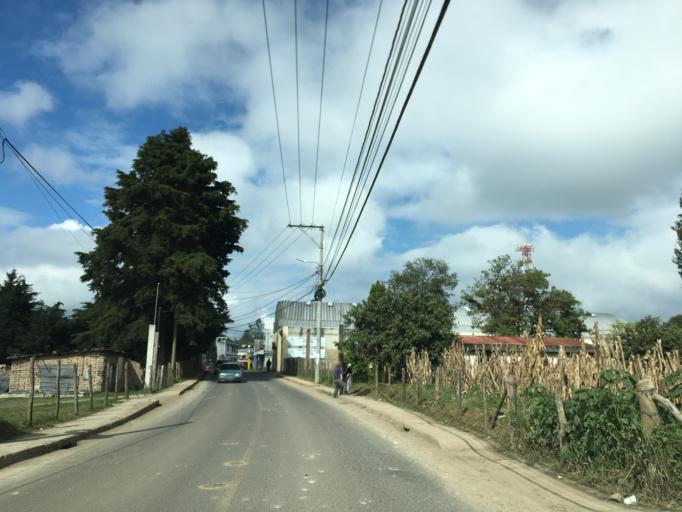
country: GT
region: Guatemala
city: San Jose Pinula
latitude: 14.5566
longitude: -90.4374
